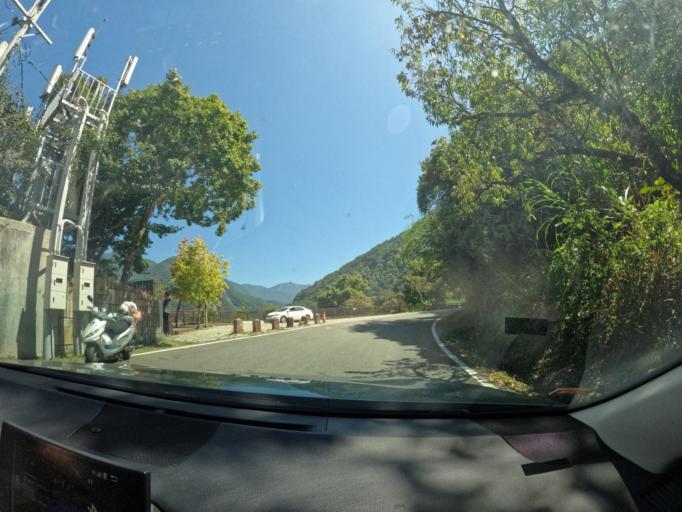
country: TW
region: Taiwan
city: Yujing
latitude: 23.2854
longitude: 120.8419
